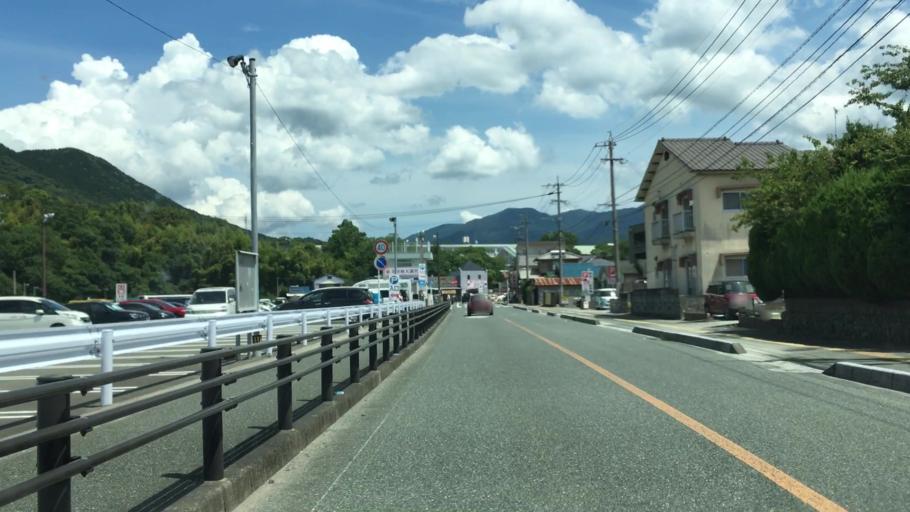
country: JP
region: Fukuoka
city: Dazaifu
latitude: 33.5180
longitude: 130.5284
